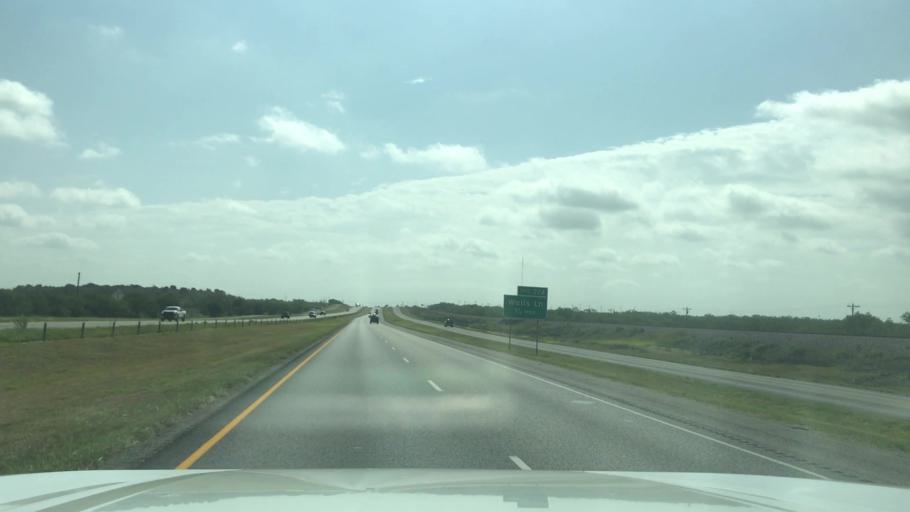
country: US
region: Texas
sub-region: Taylor County
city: Tye
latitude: 32.4613
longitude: -99.9424
